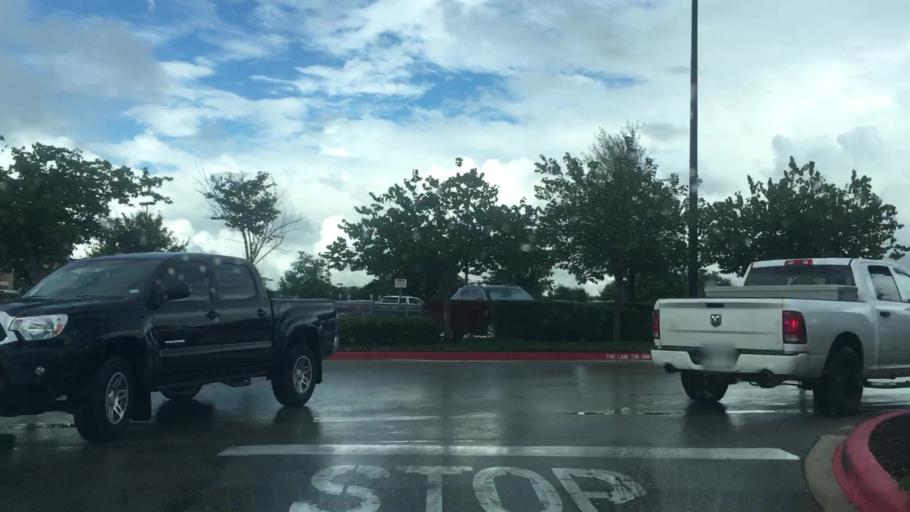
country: US
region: Texas
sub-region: Williamson County
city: Cedar Park
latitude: 30.5263
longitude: -97.8195
